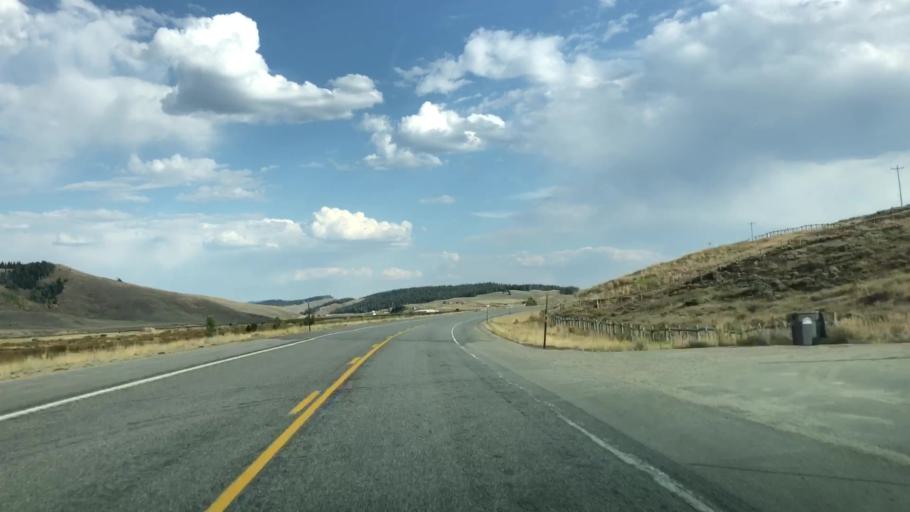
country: US
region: Wyoming
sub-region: Teton County
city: Hoback
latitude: 43.2238
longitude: -110.4297
